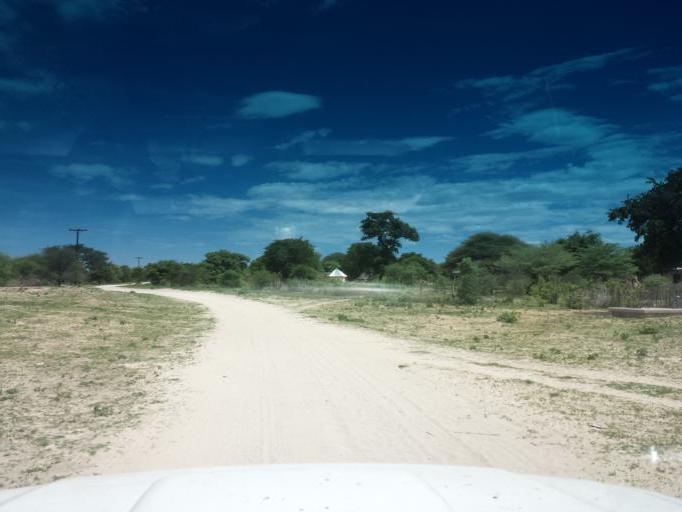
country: BW
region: North West
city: Shakawe
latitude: -18.7444
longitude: 22.1824
